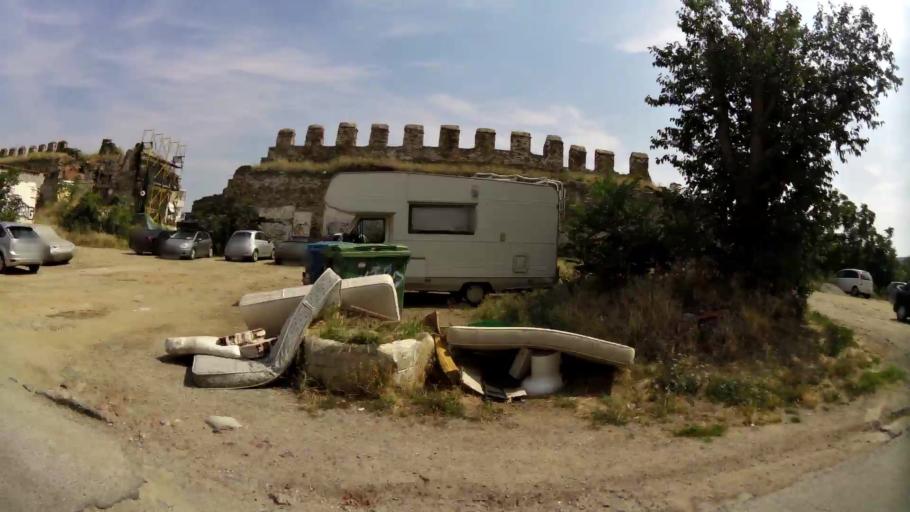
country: GR
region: Central Macedonia
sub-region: Nomos Thessalonikis
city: Sykies
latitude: 40.6430
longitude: 22.9531
